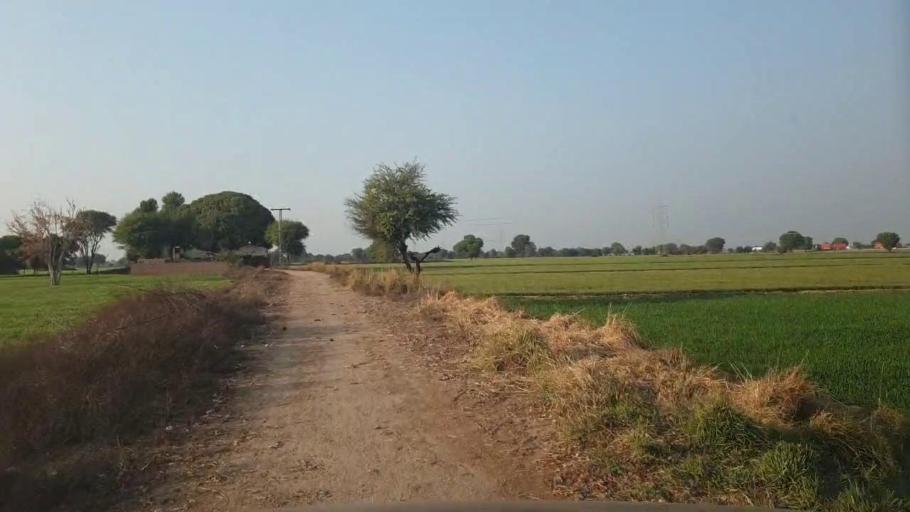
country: PK
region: Sindh
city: Hala
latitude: 25.8470
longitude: 68.4135
